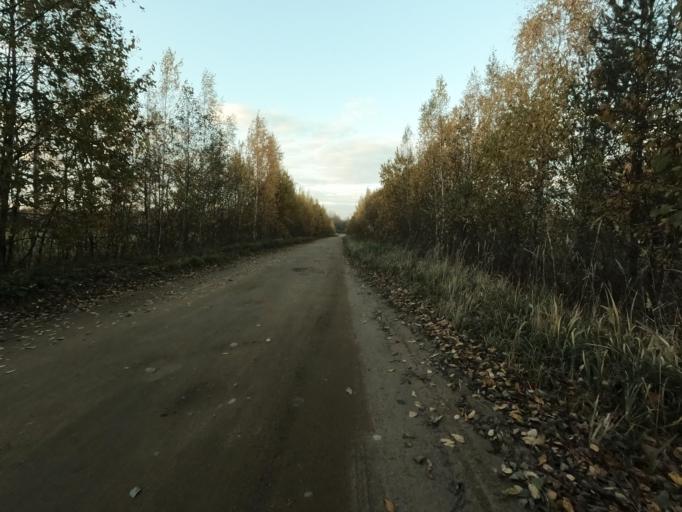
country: RU
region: Leningrad
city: Mga
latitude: 59.8039
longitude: 31.2008
